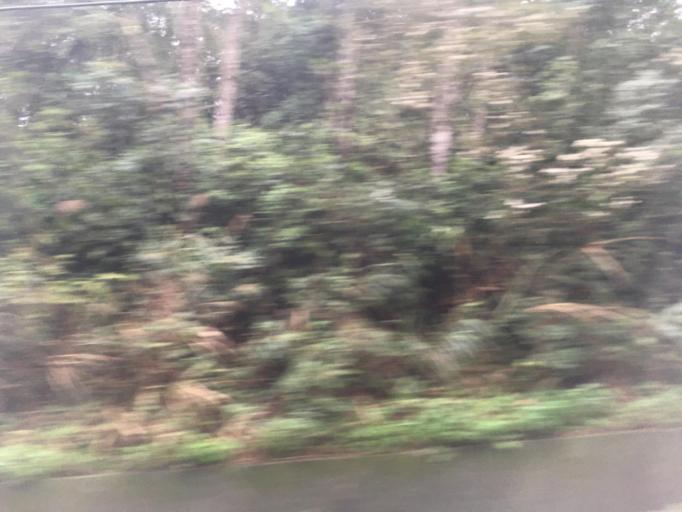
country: TW
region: Taiwan
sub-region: Miaoli
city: Miaoli
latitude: 24.4177
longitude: 120.7569
